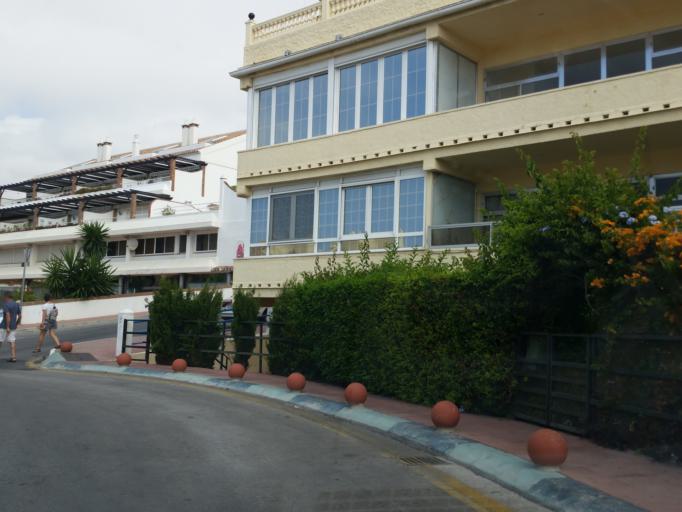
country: ES
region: Andalusia
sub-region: Provincia de Malaga
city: Torremolinos
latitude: 36.5986
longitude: -4.5124
